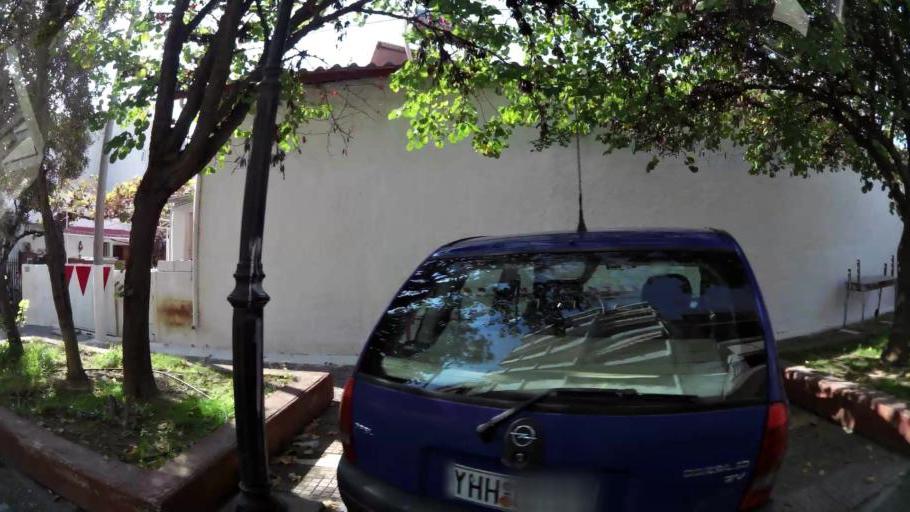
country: GR
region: Attica
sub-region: Nomarchia Athinas
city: Kamateron
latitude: 38.0588
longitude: 23.7117
